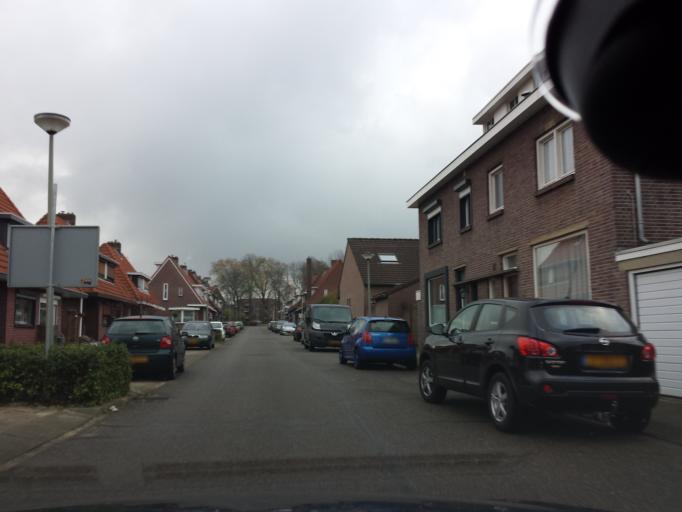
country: NL
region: Limburg
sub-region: Gemeente Kerkrade
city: Kerkrade
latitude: 50.9145
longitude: 6.0441
